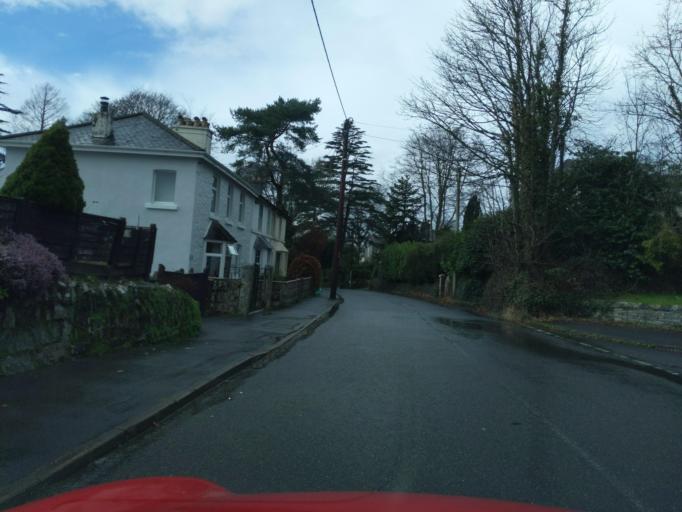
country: GB
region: England
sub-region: Devon
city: Tavistock
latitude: 50.5350
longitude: -4.1322
